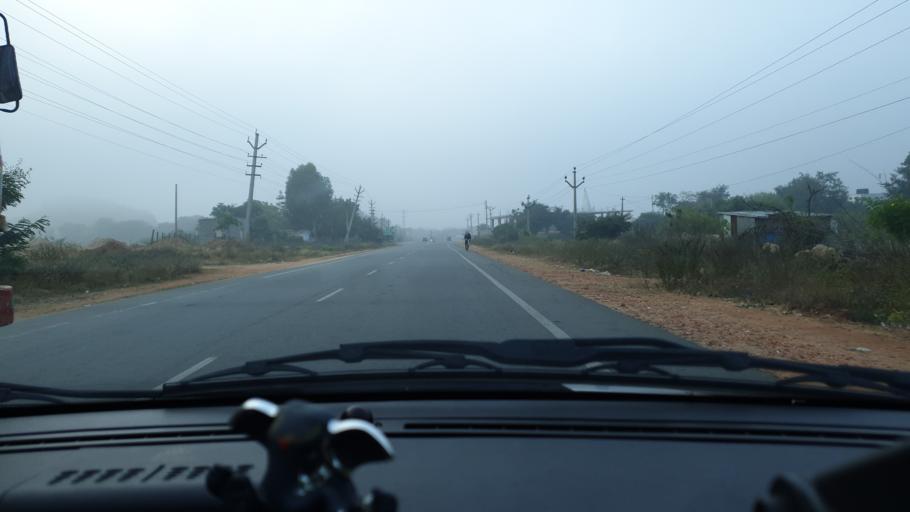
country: IN
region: Telangana
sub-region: Mahbubnagar
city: Farrukhnagar
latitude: 16.8653
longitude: 78.5288
